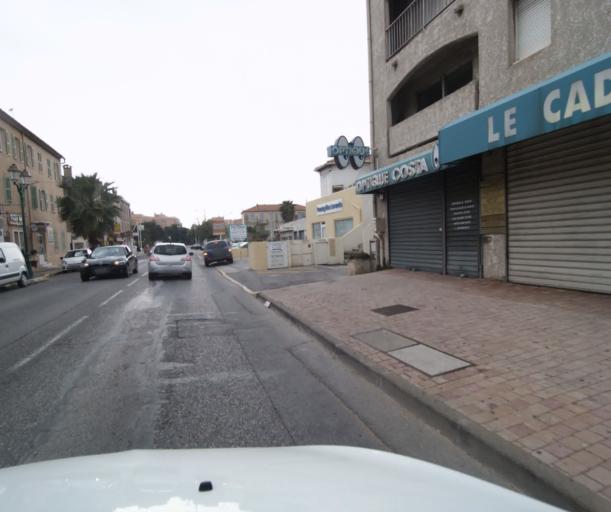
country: FR
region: Provence-Alpes-Cote d'Azur
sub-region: Departement du Var
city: Le Pradet
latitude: 43.1068
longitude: 6.0176
